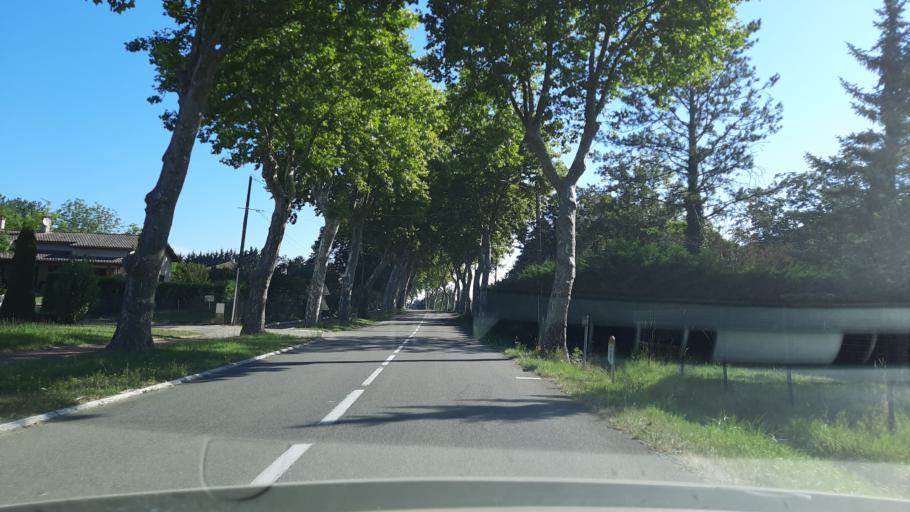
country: FR
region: Midi-Pyrenees
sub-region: Departement du Tarn-et-Garonne
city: Molieres
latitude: 44.1947
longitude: 1.3696
